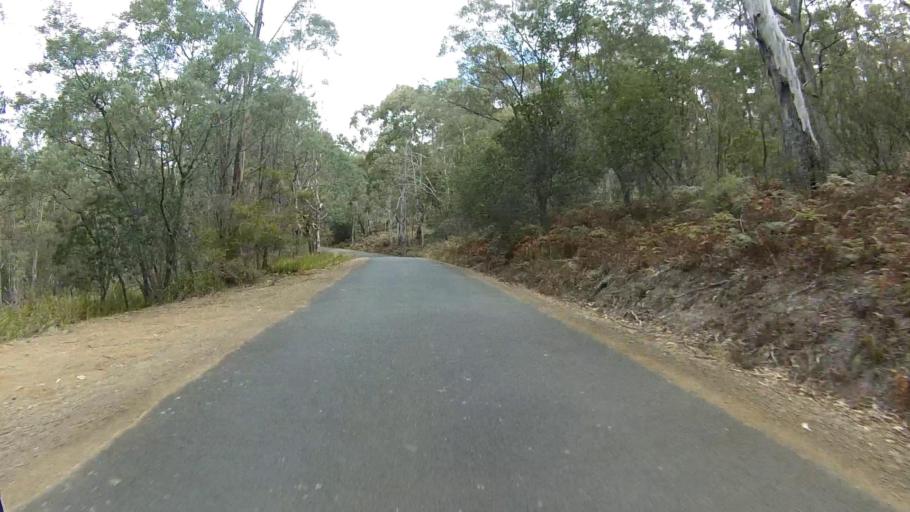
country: AU
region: Tasmania
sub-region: Sorell
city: Sorell
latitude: -42.6023
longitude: 147.9223
